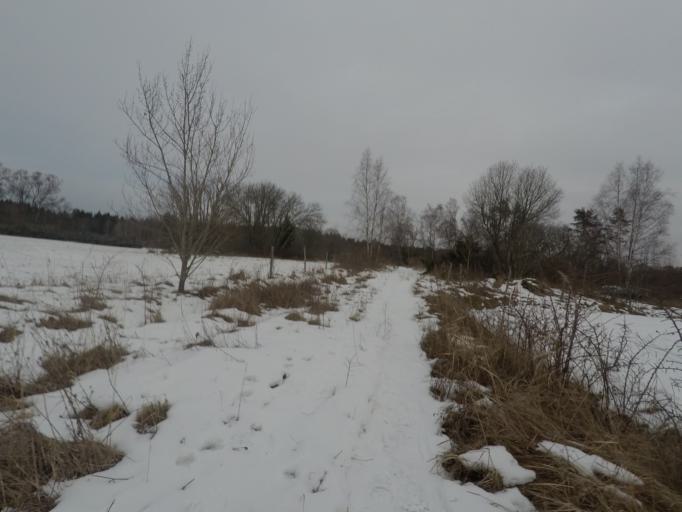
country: SE
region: Soedermanland
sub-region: Eskilstuna Kommun
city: Kvicksund
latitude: 59.4466
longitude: 16.3576
